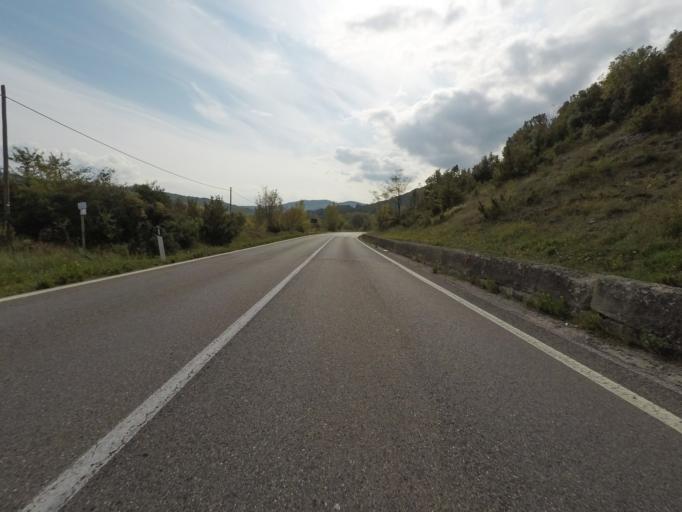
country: IT
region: Tuscany
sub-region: Provincia di Siena
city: Murlo
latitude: 43.1372
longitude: 11.2901
